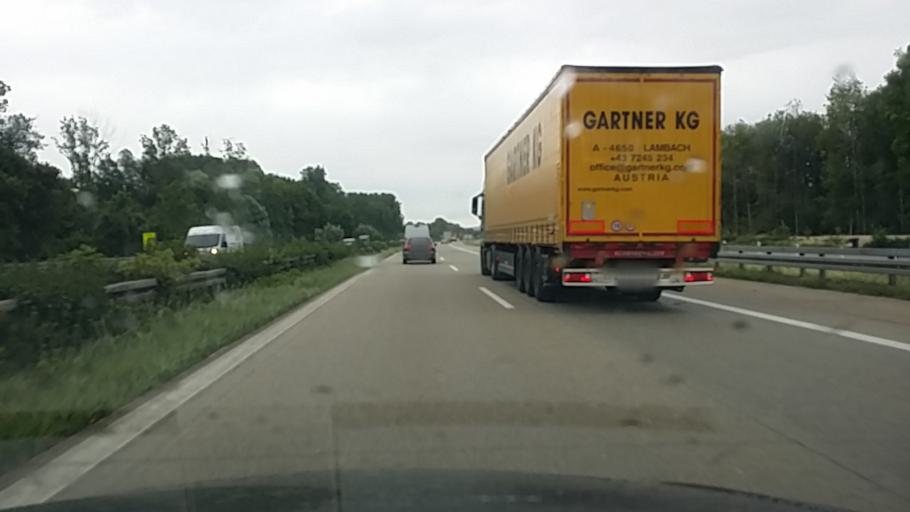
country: DE
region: Bavaria
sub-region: Lower Bavaria
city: Niederalteich
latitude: 48.7881
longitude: 13.0108
